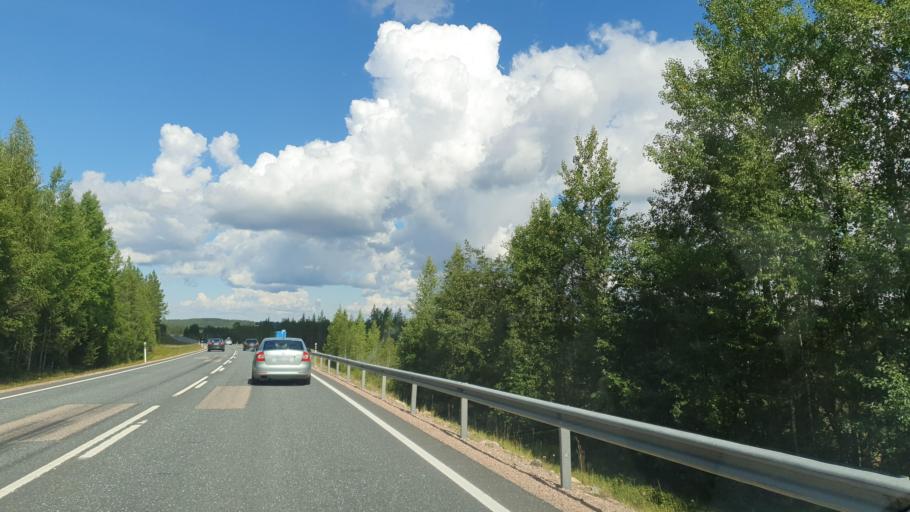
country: FI
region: Kainuu
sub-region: Kajaani
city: Kajaani
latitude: 64.0593
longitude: 27.4560
